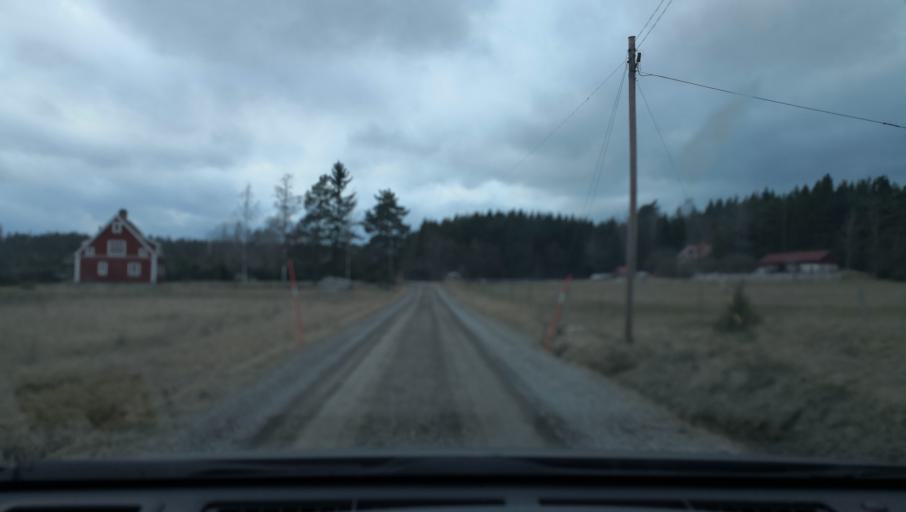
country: SE
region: Vaestmanland
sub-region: Kopings Kommun
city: Kolsva
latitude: 59.5633
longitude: 15.8326
